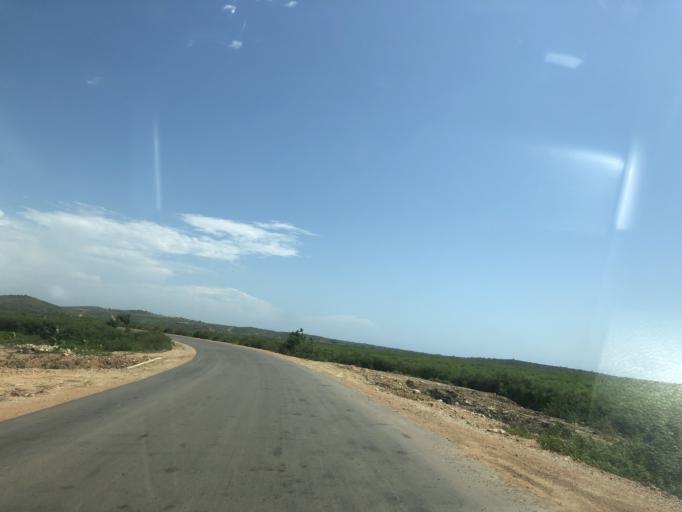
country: AO
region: Cuanza Sul
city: Sumbe
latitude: -10.8780
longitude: 13.8393
